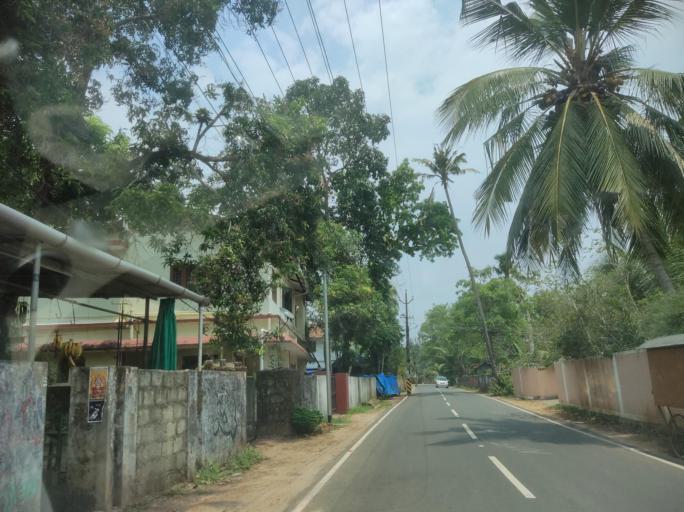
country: IN
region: Kerala
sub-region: Alappuzha
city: Vayalar
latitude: 9.7121
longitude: 76.3259
